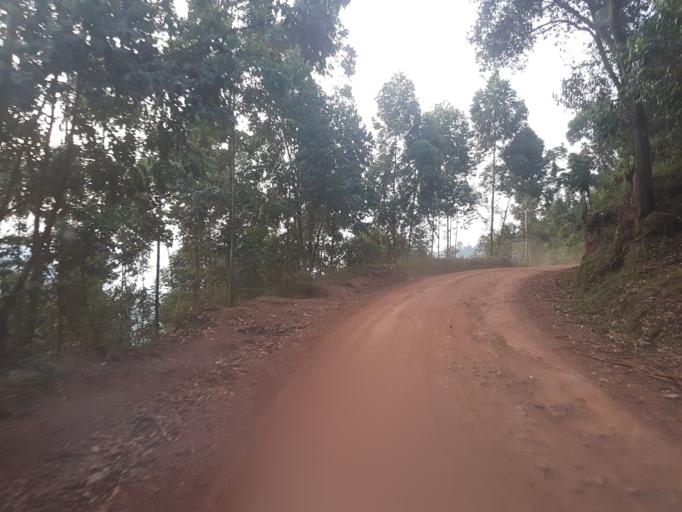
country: UG
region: Western Region
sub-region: Kanungu District
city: Kanungu
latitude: -0.9638
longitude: 29.8365
